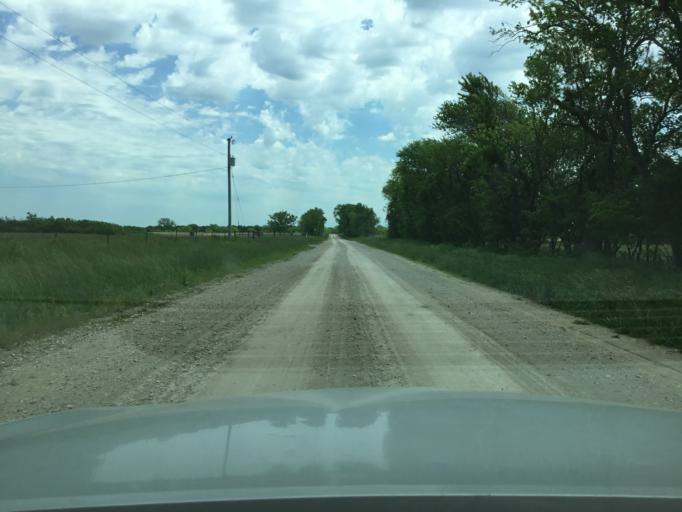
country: US
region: Kansas
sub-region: Montgomery County
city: Caney
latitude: 37.0951
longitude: -95.8029
